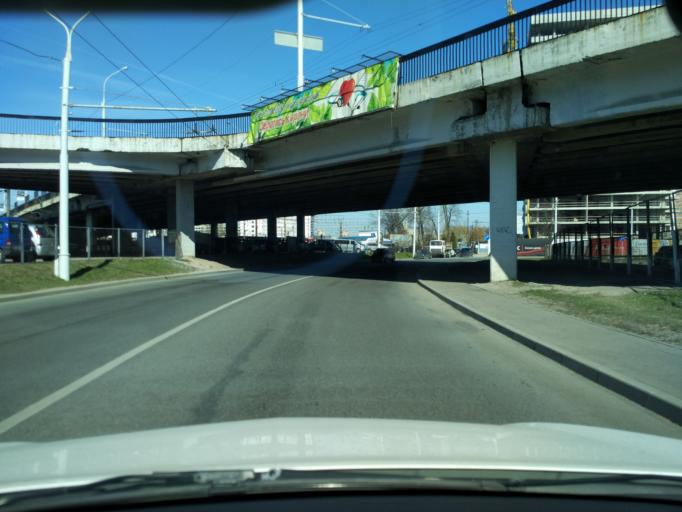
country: BY
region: Minsk
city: Minsk
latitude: 53.8834
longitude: 27.5362
